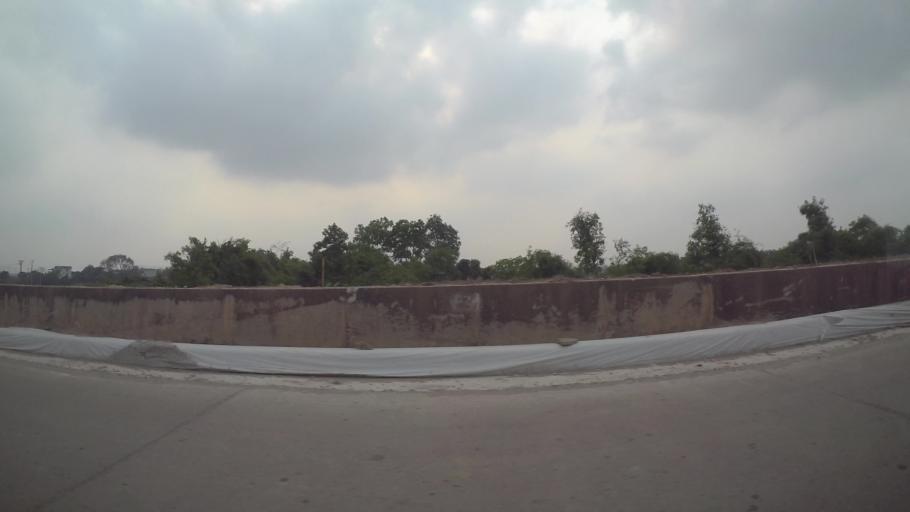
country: VN
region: Ha Noi
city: Trau Quy
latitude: 21.0145
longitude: 105.9046
